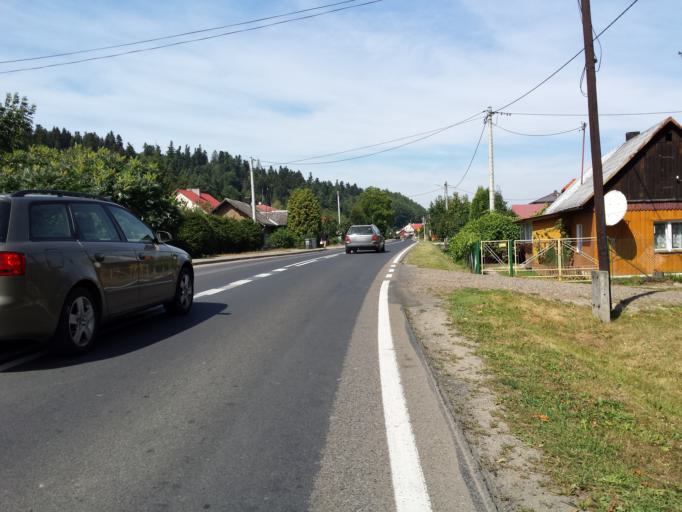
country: PL
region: Subcarpathian Voivodeship
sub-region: Powiat leski
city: Lesko
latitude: 49.4647
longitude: 22.3239
